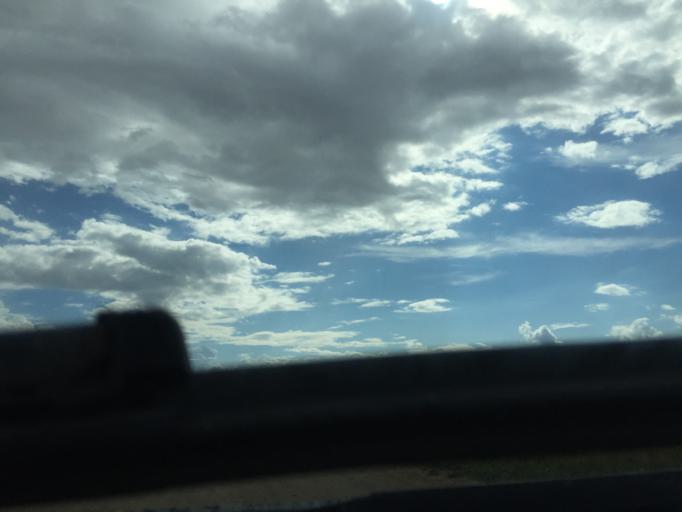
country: LT
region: Siauliu apskritis
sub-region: Joniskis
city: Joniskis
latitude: 56.3299
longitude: 23.5609
